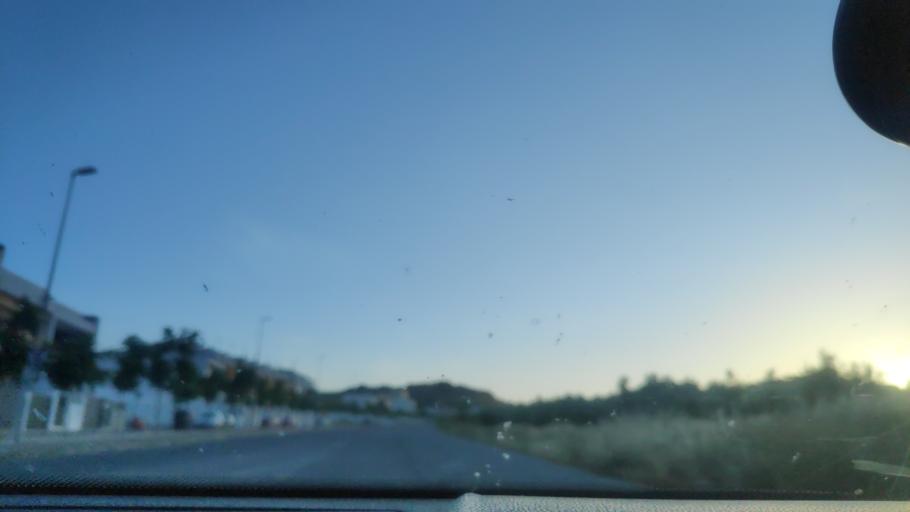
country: ES
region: Andalusia
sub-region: Provincia de Jaen
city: Jaen
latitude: 37.7840
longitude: -3.8155
